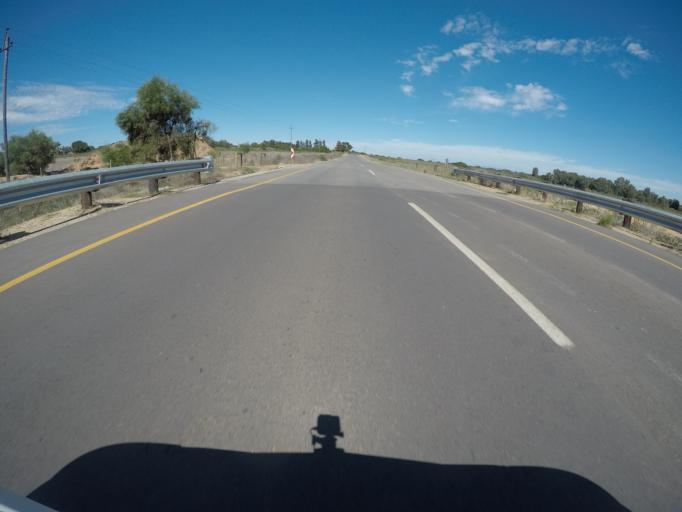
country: ZA
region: Western Cape
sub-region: West Coast District Municipality
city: Malmesbury
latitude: -33.5836
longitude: 18.6468
